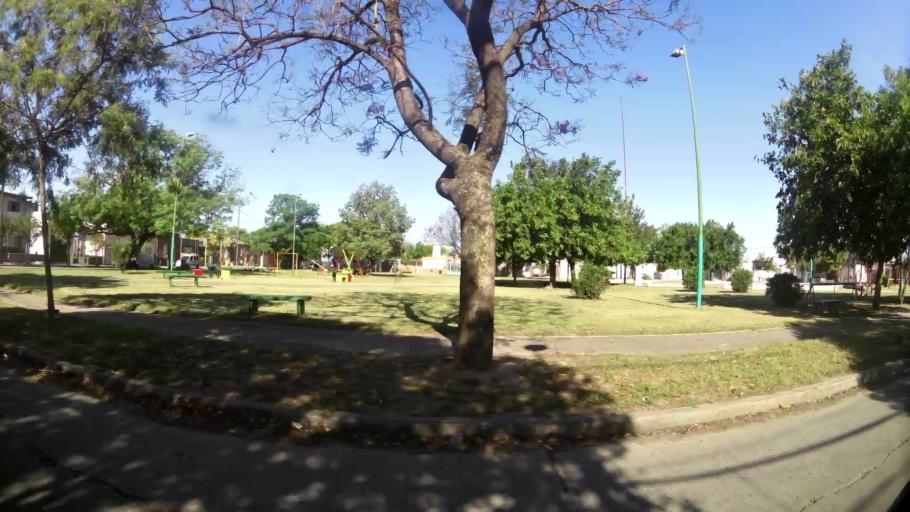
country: AR
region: Cordoba
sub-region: Departamento de Capital
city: Cordoba
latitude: -31.3917
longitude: -64.1341
